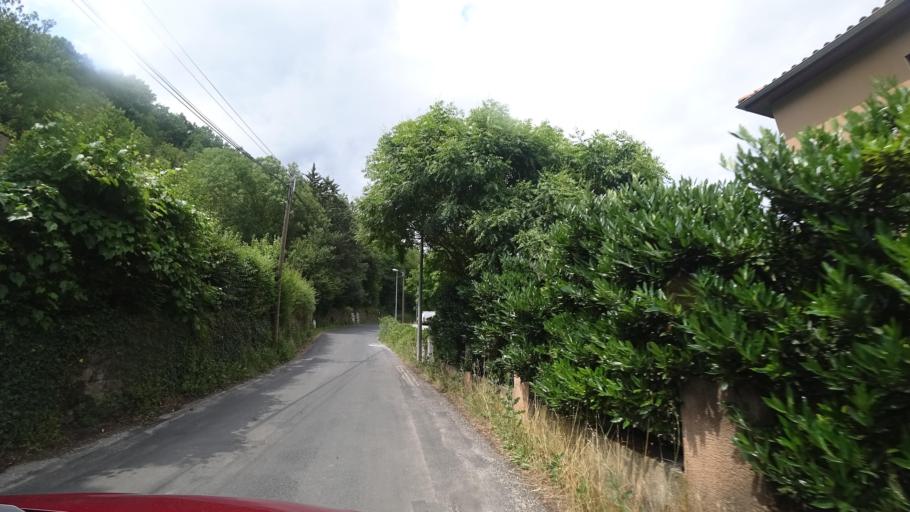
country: FR
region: Midi-Pyrenees
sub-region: Departement de l'Aveyron
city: Saint-Affrique
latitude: 43.9484
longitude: 2.8915
